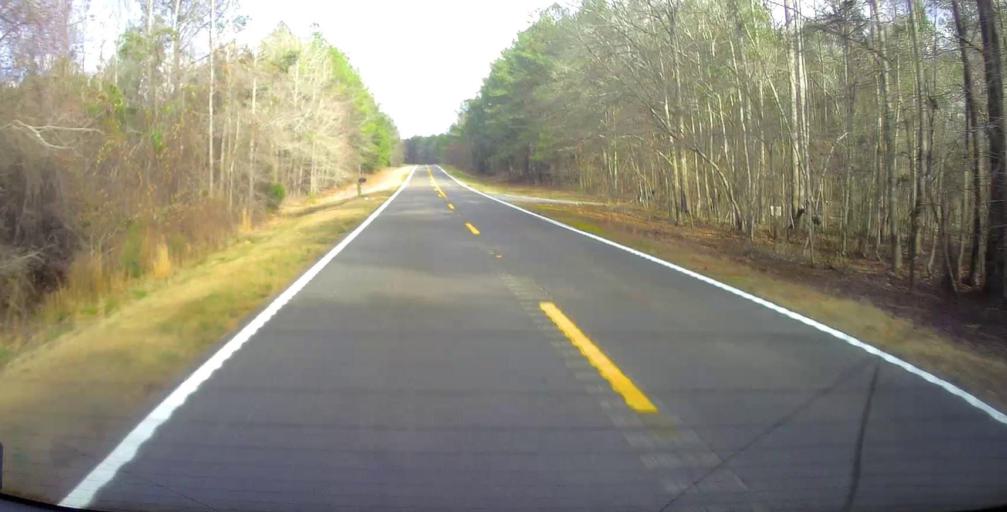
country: US
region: Georgia
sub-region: Marion County
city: Buena Vista
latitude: 32.4412
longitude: -84.4838
